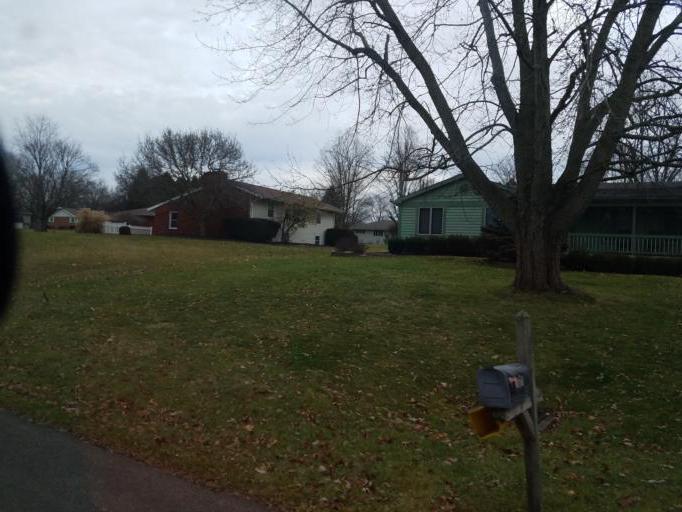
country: US
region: Ohio
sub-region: Marion County
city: Marion
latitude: 40.5654
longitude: -83.0799
